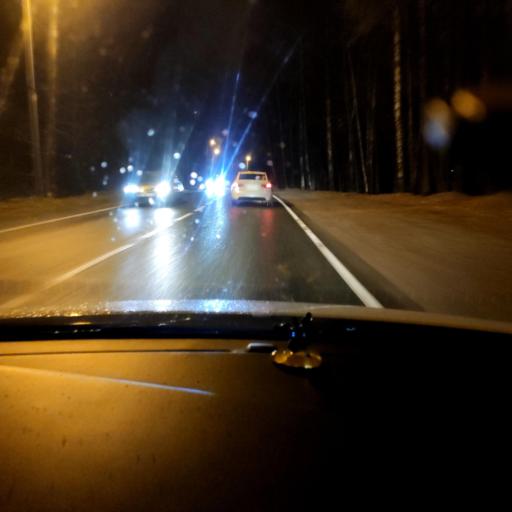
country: RU
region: Tatarstan
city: Osinovo
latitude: 55.8395
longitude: 48.8933
